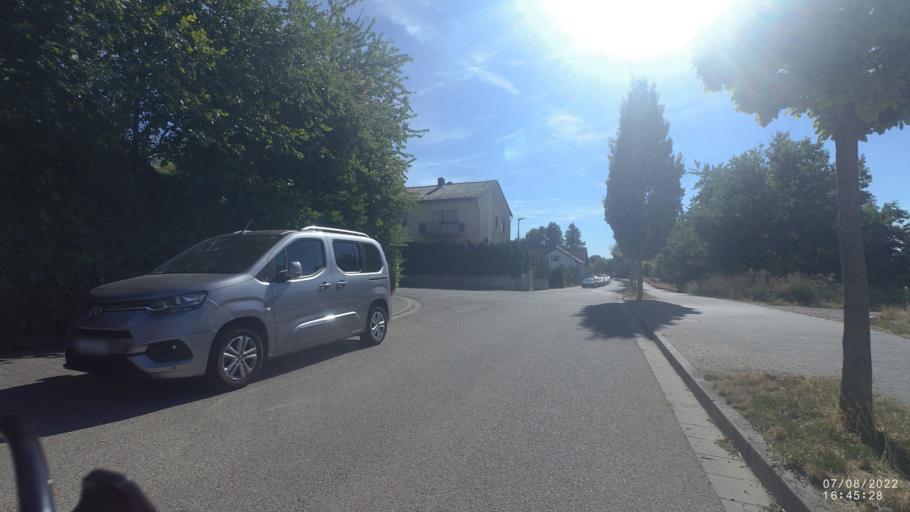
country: DE
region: Rheinland-Pfalz
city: Ober-Saulheim
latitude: 49.8666
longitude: 8.1385
